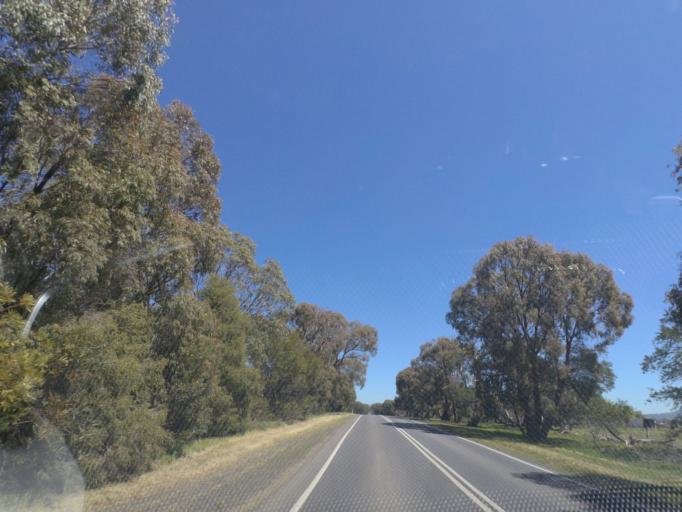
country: AU
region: Victoria
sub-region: Whittlesea
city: Whittlesea
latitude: -37.2934
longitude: 144.9268
